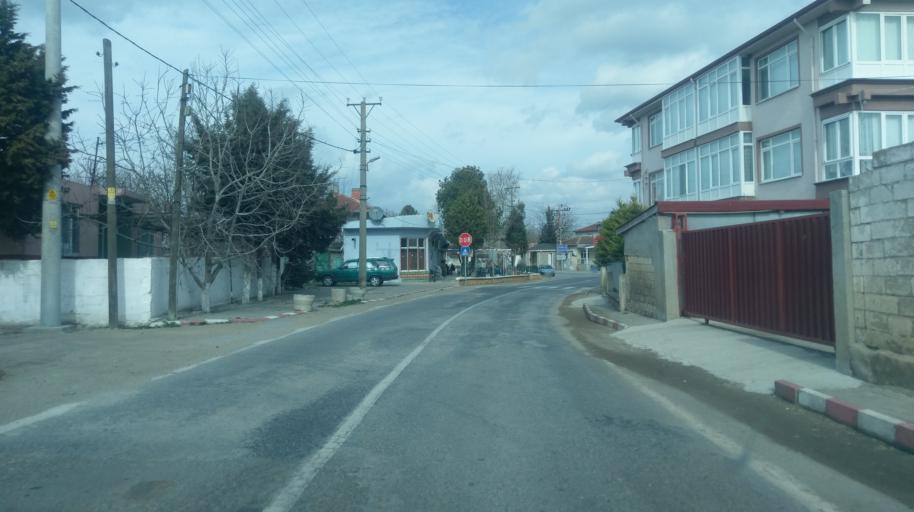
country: TR
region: Edirne
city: Haskoy
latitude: 41.6408
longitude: 26.8578
